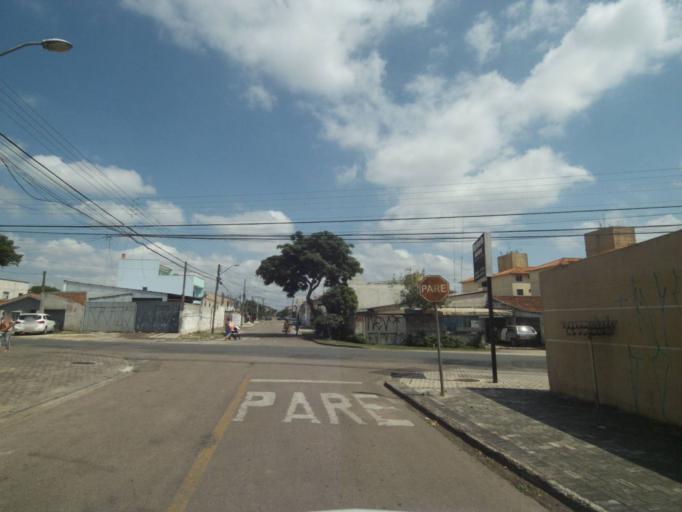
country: BR
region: Parana
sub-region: Sao Jose Dos Pinhais
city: Sao Jose dos Pinhais
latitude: -25.5447
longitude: -49.2553
